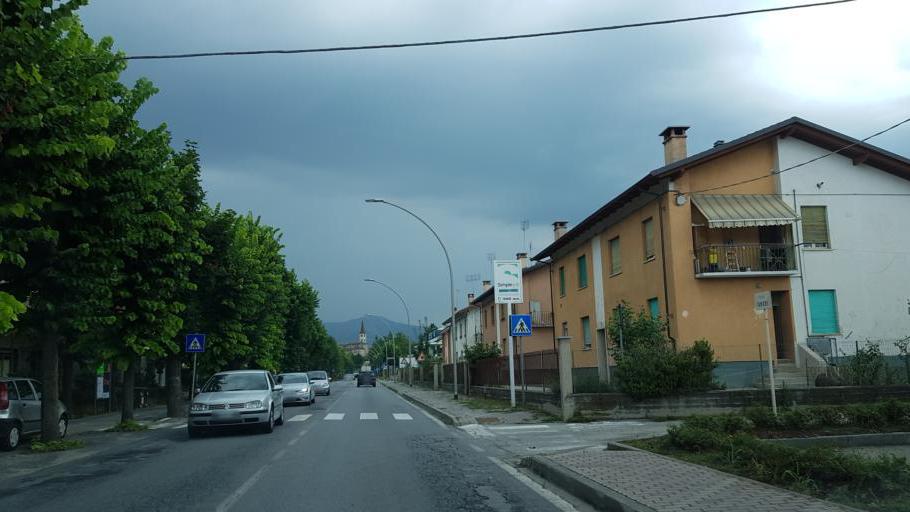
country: IT
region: Piedmont
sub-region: Provincia di Cuneo
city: Caraglio
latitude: 44.4151
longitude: 7.4362
